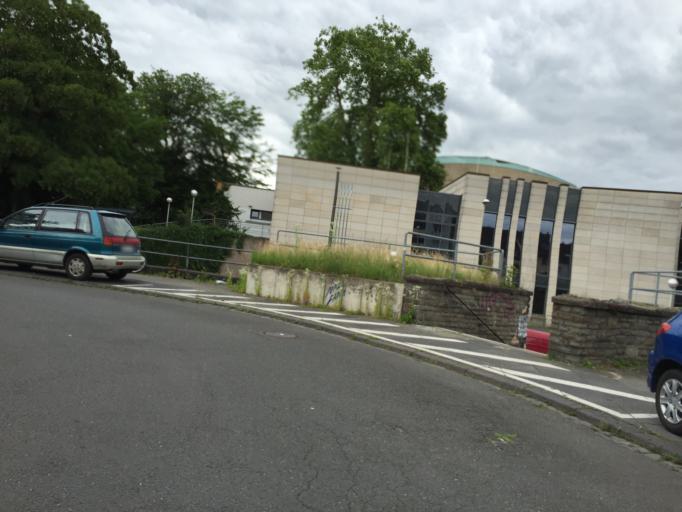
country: DE
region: North Rhine-Westphalia
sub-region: Regierungsbezirk Koln
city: Bonn
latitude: 50.7400
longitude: 7.1050
